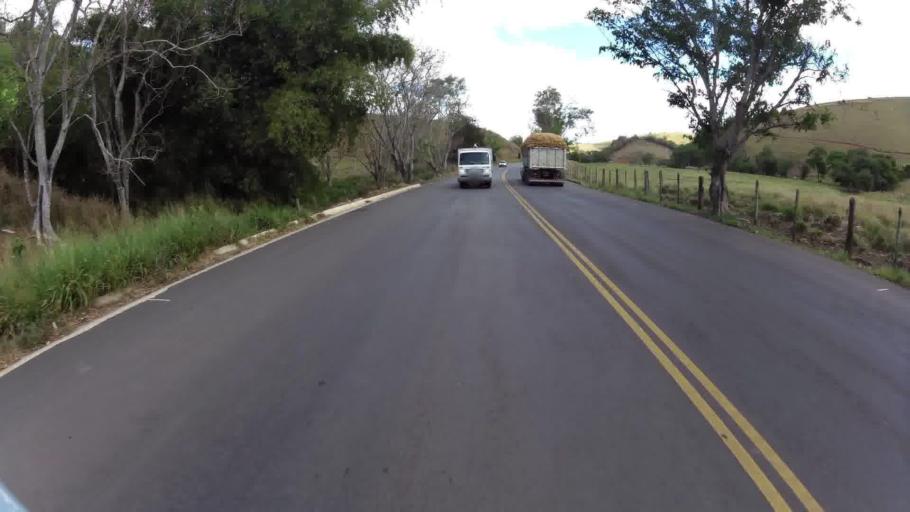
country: BR
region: Rio de Janeiro
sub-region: Cambuci
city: Cambuci
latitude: -21.3867
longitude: -41.9657
